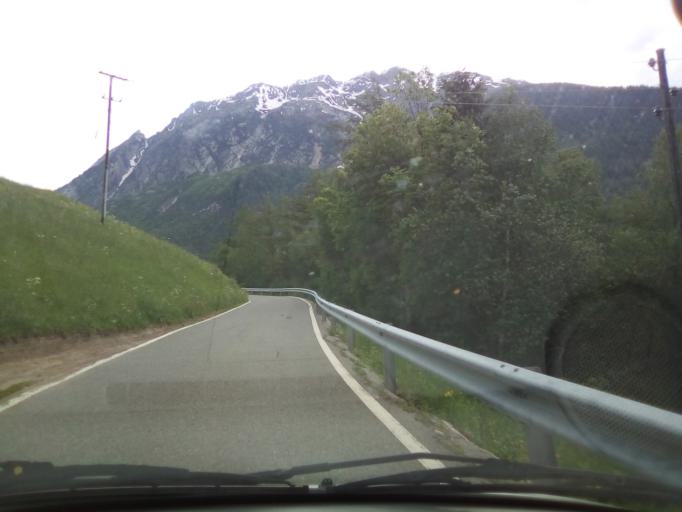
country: CH
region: Valais
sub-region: Entremont District
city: Orsieres
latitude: 46.0620
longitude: 7.1537
